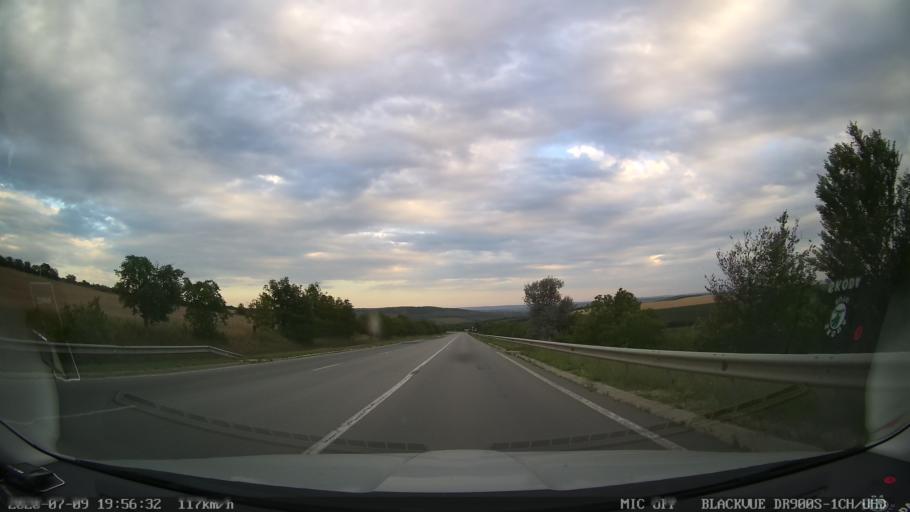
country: MD
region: Orhei
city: Orhei
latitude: 47.5290
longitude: 28.7954
